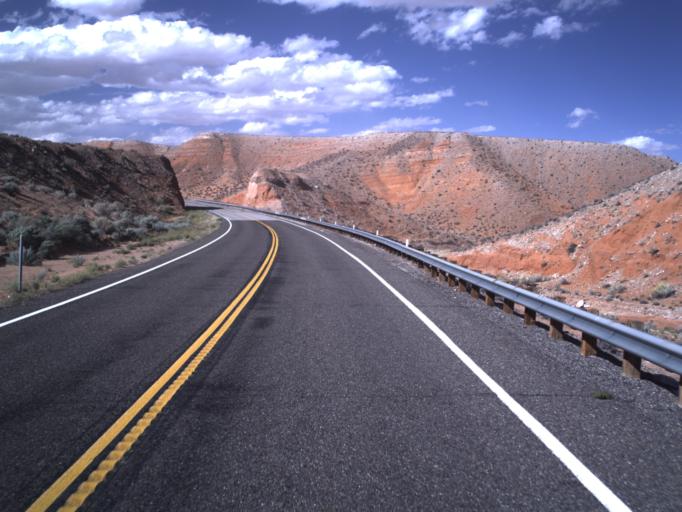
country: US
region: Utah
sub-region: Wayne County
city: Loa
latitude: 38.1391
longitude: -110.6095
